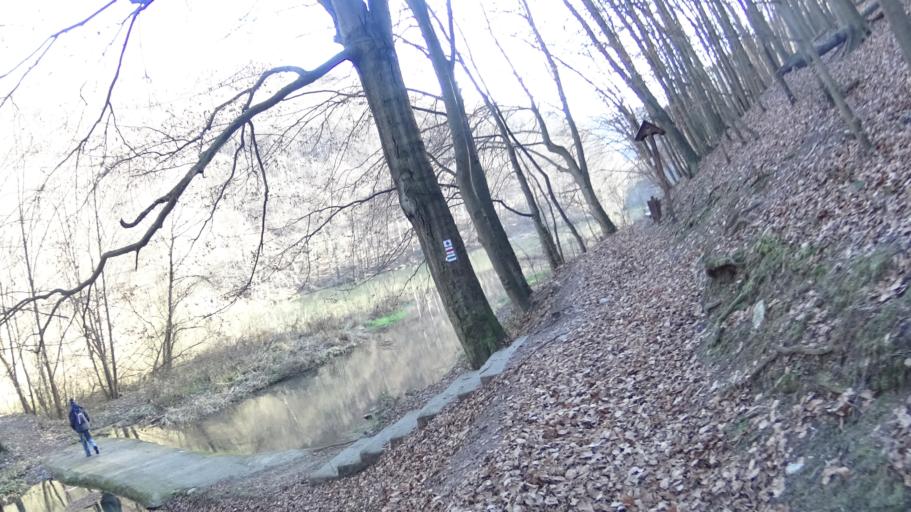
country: HU
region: Borsod-Abauj-Zemplen
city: Sajobabony
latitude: 48.1108
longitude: 20.6136
